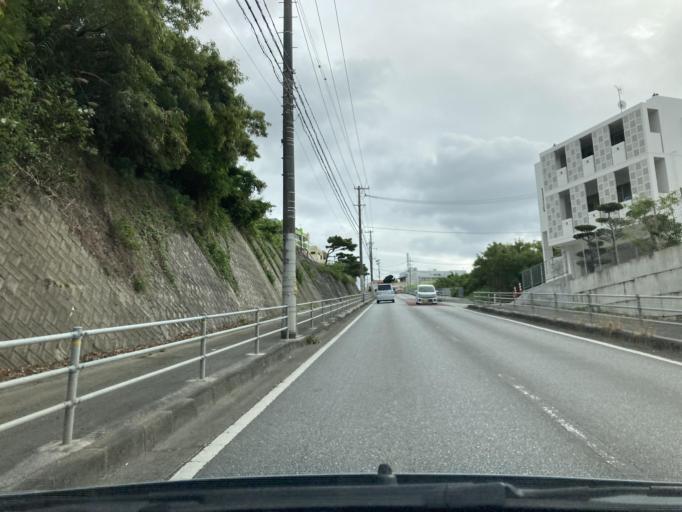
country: JP
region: Okinawa
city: Tomigusuku
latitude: 26.1631
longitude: 127.6795
